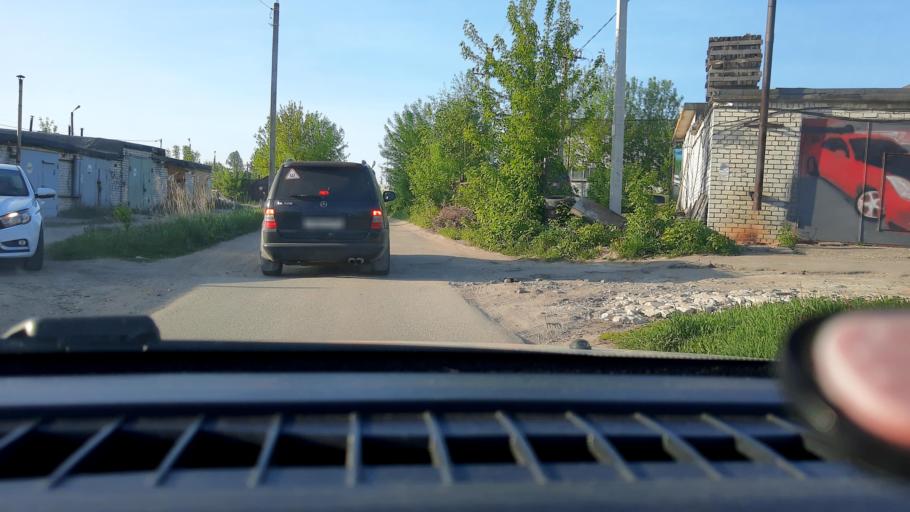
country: RU
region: Nizjnij Novgorod
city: Kstovo
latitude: 56.1338
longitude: 44.1912
